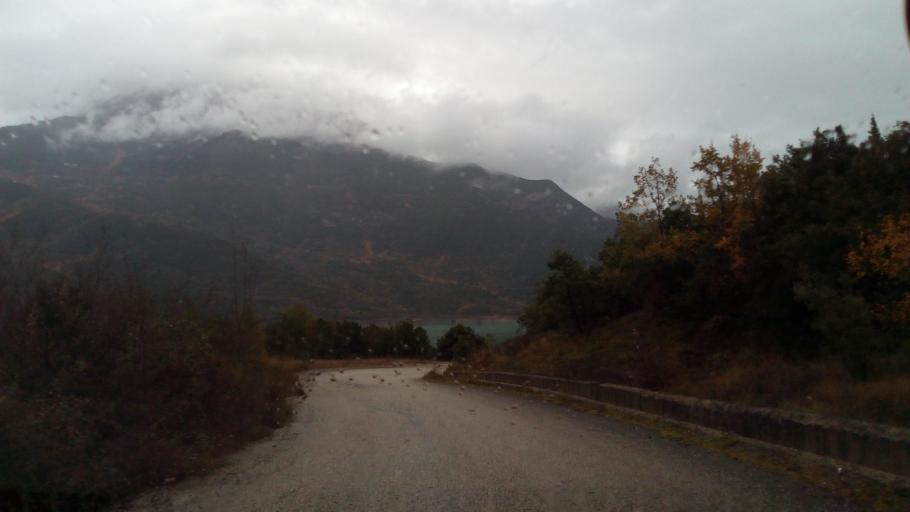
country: GR
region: West Greece
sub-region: Nomos Aitolias kai Akarnanias
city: Thermo
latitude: 38.6589
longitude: 21.8560
